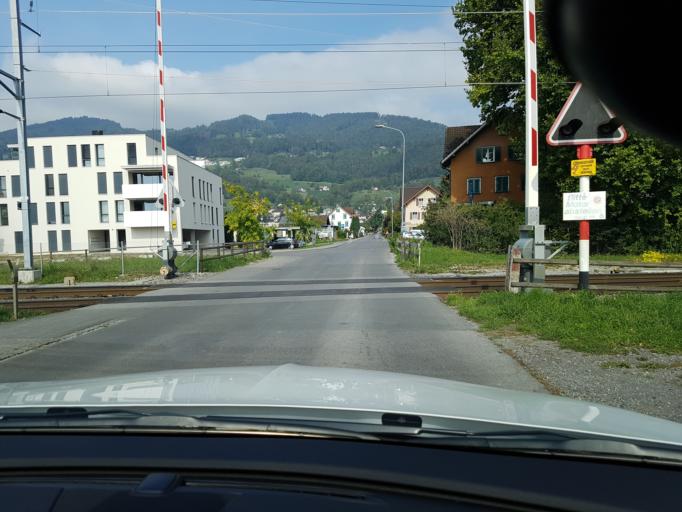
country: CH
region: Saint Gallen
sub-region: Wahlkreis Rheintal
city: Rebstein
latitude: 47.3930
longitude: 9.5882
